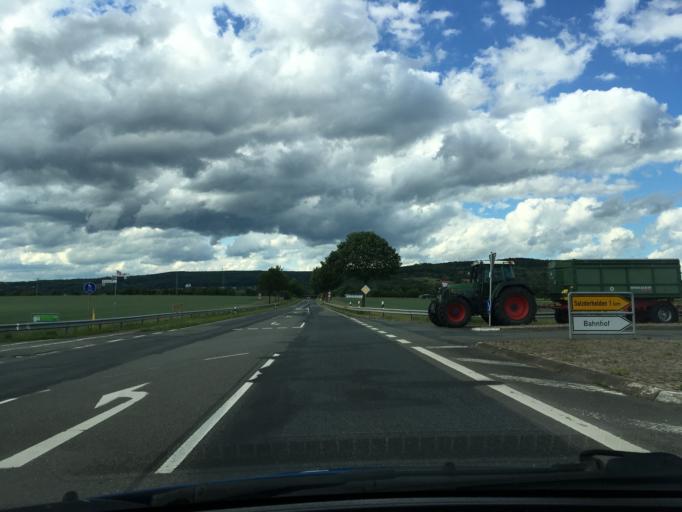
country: DE
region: Lower Saxony
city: Einbeck
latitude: 51.7989
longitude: 9.8982
